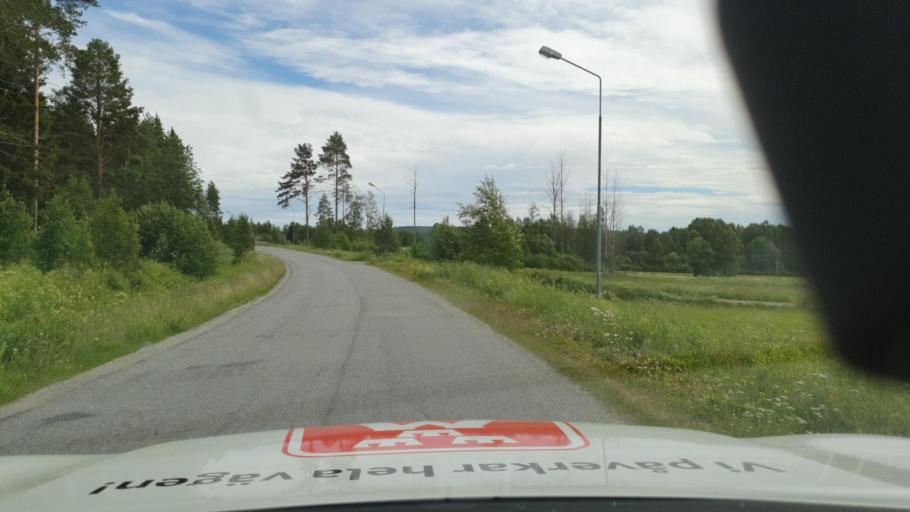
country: SE
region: Vaesterbotten
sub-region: Skelleftea Kommun
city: Burtraesk
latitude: 64.4857
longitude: 20.5075
